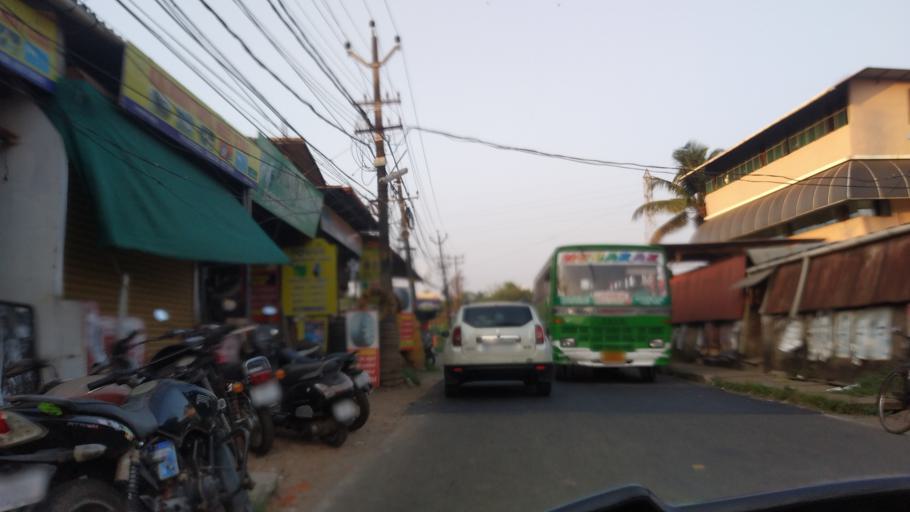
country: IN
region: Kerala
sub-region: Ernakulam
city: Elur
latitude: 10.0276
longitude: 76.2750
